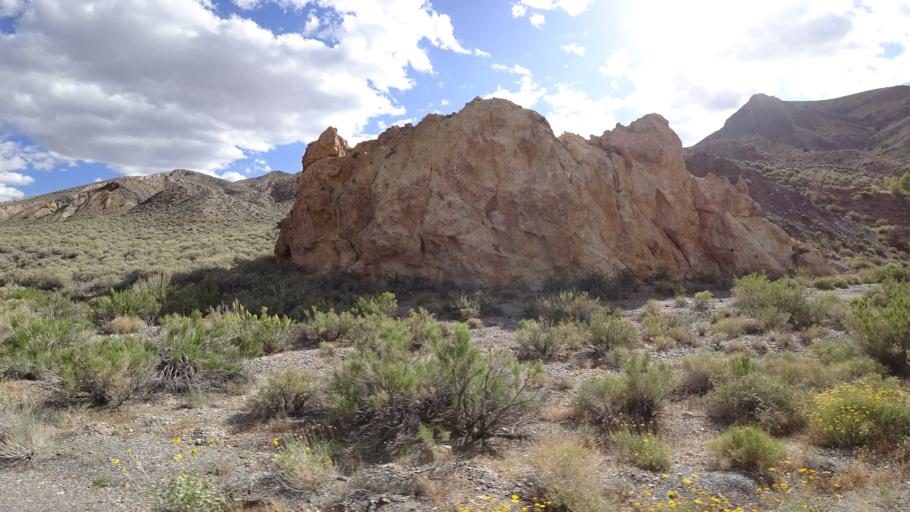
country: US
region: Nevada
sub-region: Nye County
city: Beatty
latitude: 36.4251
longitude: -117.1923
